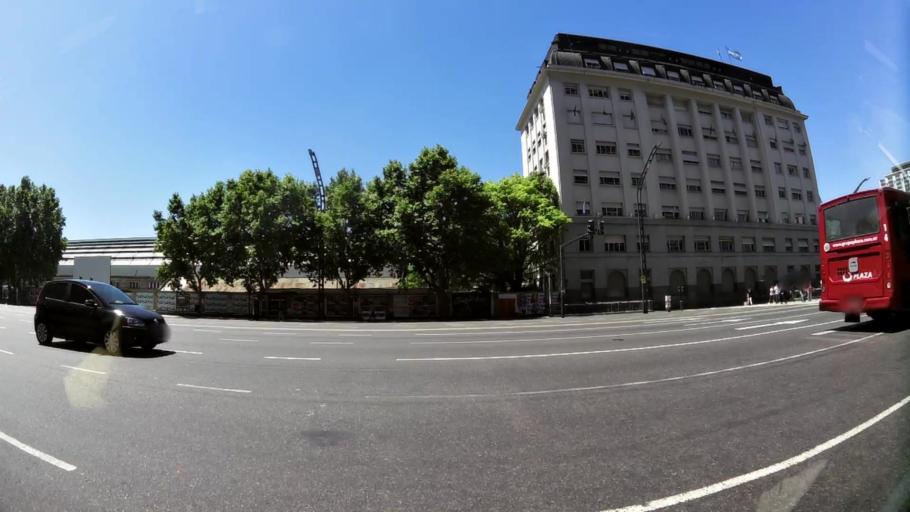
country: AR
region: Buenos Aires F.D.
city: Retiro
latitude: -34.5924
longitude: -58.3762
